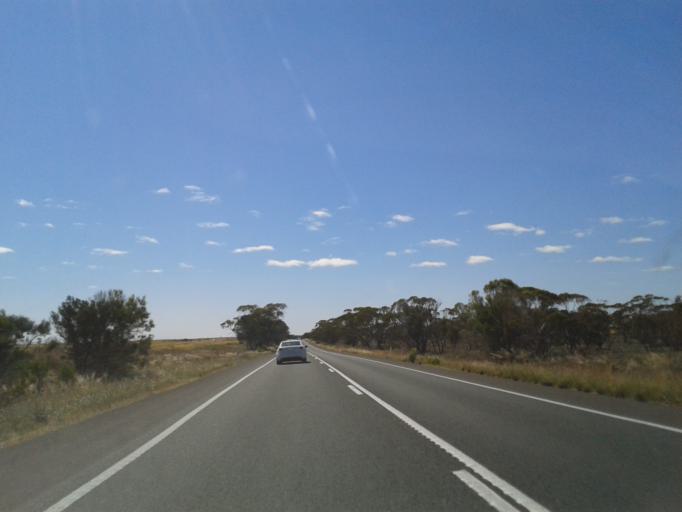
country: AU
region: New South Wales
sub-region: Wentworth
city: Dareton
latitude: -34.2551
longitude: 141.8897
